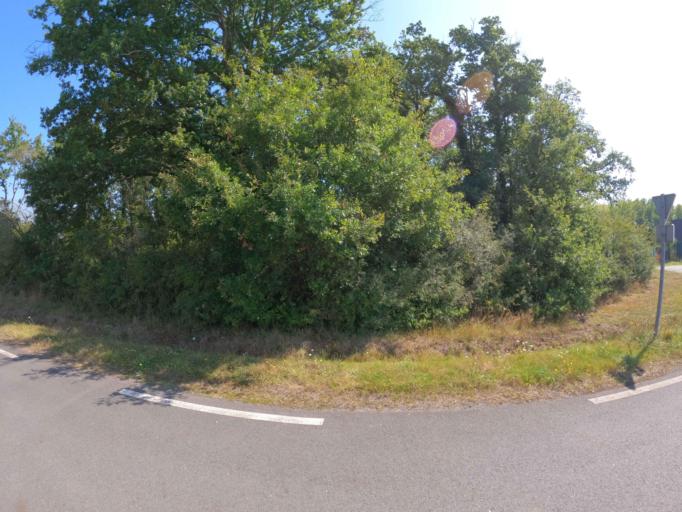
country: FR
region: Pays de la Loire
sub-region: Departement de la Loire-Atlantique
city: Geneston
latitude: 47.0653
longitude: -1.5013
